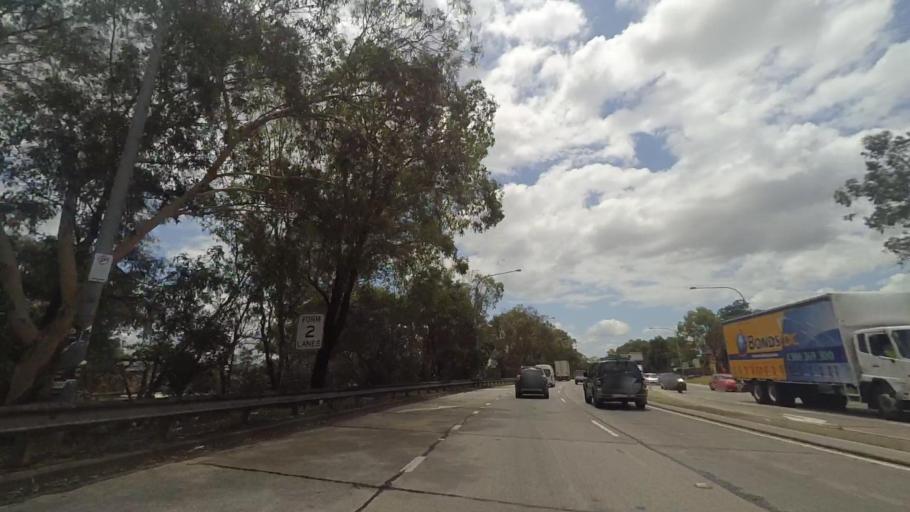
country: AU
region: New South Wales
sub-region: Fairfield
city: Cabramatta West
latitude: -33.8987
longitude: 150.9194
